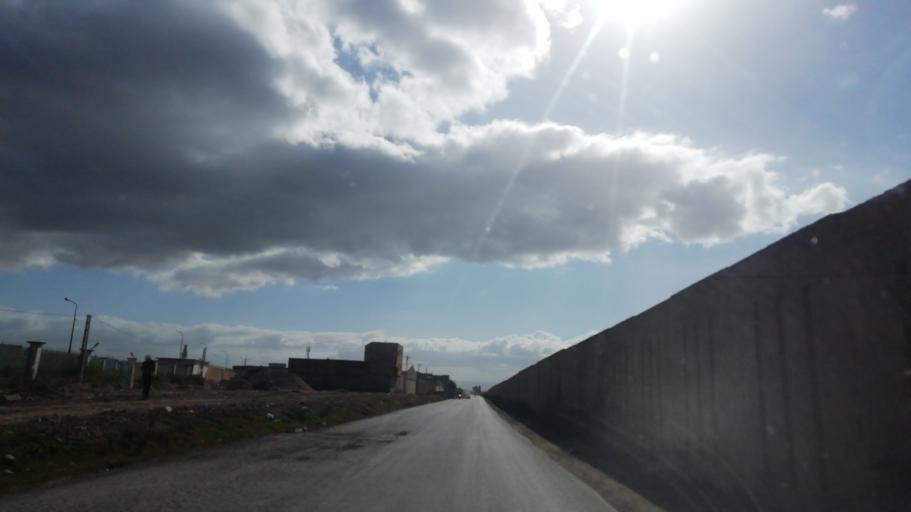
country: DZ
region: Oran
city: Es Senia
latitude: 35.6476
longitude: -0.6056
